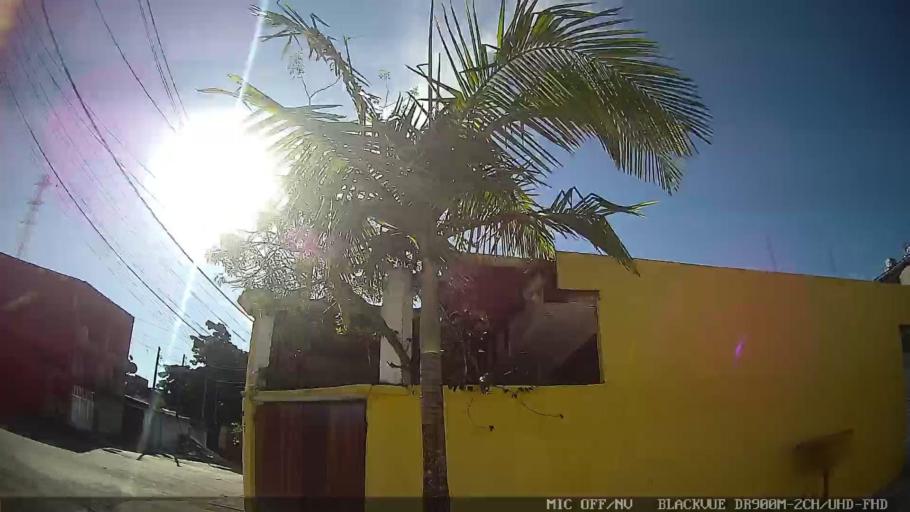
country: BR
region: Sao Paulo
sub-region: Guaruja
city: Guaruja
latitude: -23.9489
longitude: -46.2816
